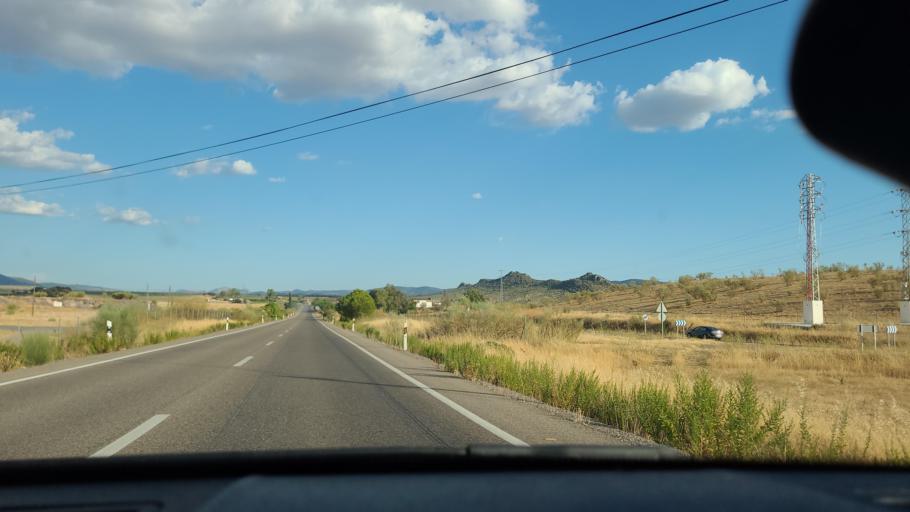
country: ES
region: Andalusia
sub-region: Province of Cordoba
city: Belmez
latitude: 38.2724
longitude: -5.1944
